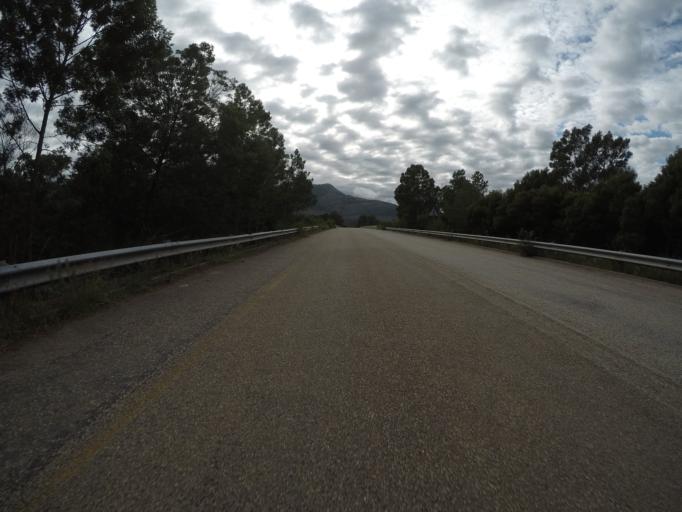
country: ZA
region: Eastern Cape
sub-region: Cacadu District Municipality
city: Kareedouw
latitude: -34.0141
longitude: 24.3062
